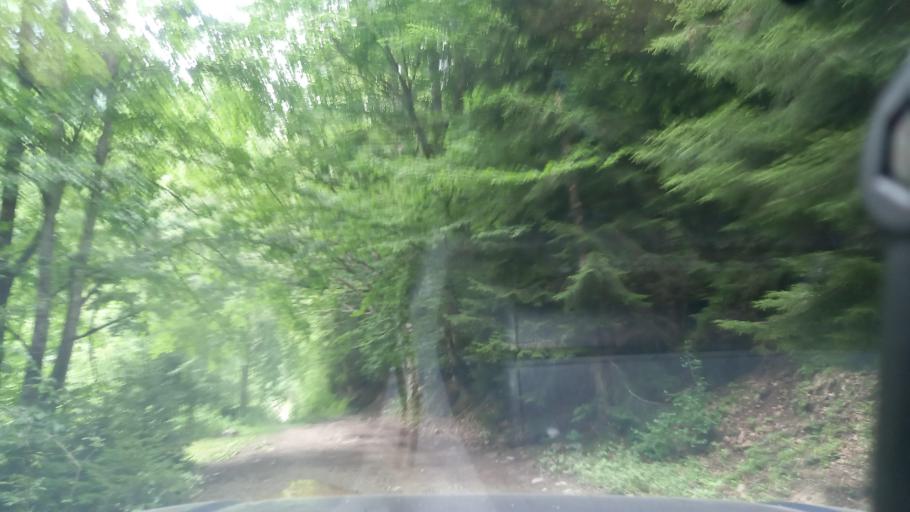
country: RU
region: Karachayevo-Cherkesiya
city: Kurdzhinovo
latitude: 43.8183
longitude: 40.8965
